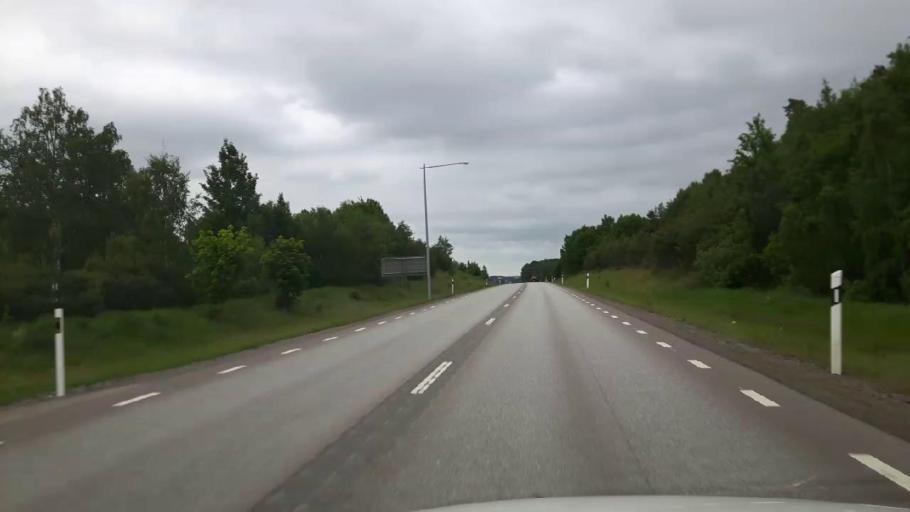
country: SE
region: Vaestmanland
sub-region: Kopings Kommun
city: Koping
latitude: 59.5425
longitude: 15.9347
